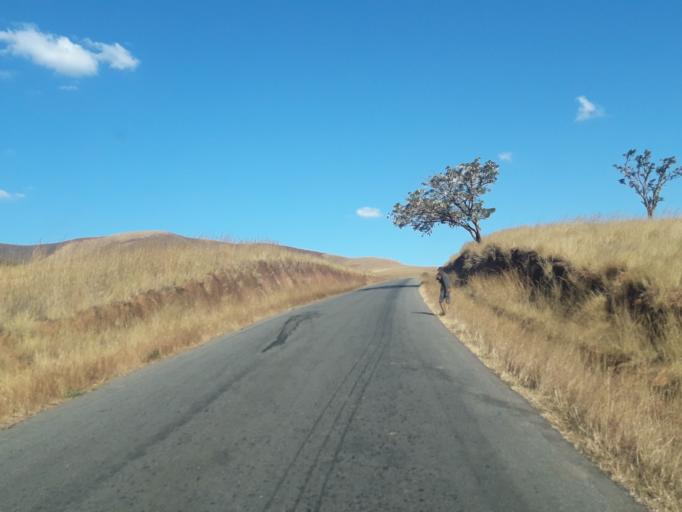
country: MG
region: Betsiboka
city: Maevatanana
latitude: -17.6273
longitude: 46.9540
